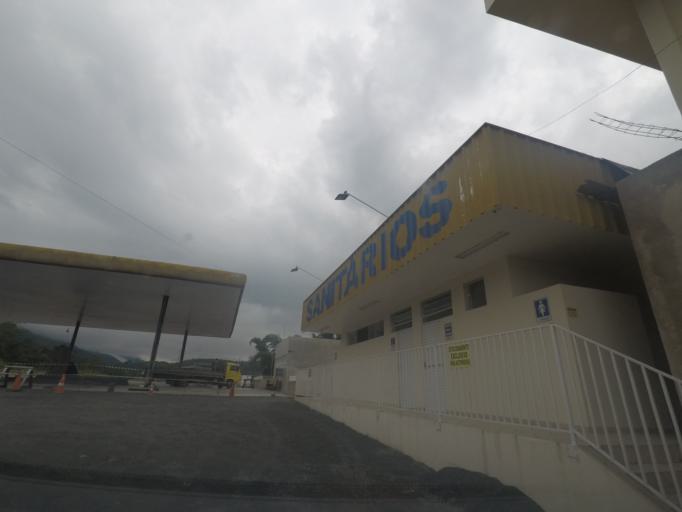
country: BR
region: Parana
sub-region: Campina Grande Do Sul
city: Campina Grande do Sul
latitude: -25.1207
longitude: -48.8559
